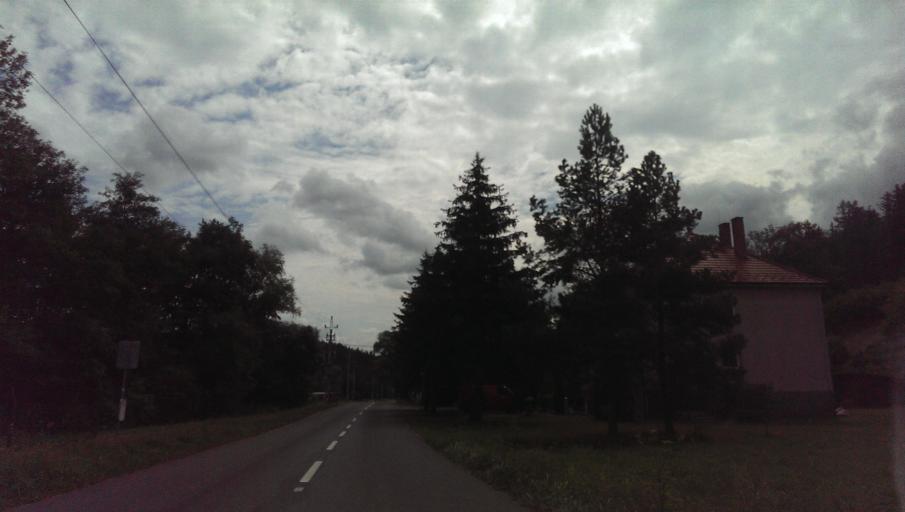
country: CZ
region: South Moravian
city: Velka nad Velickou
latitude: 48.8946
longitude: 17.5754
